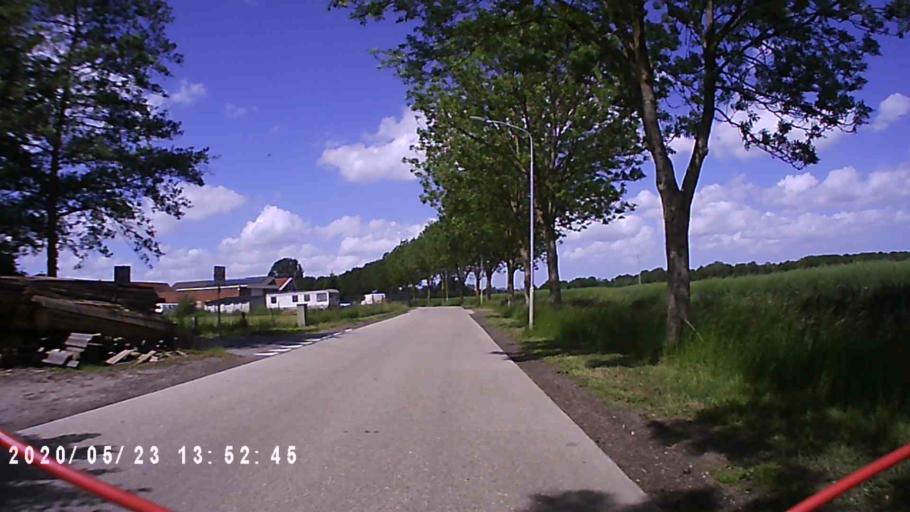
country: NL
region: Groningen
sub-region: Gemeente  Oldambt
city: Winschoten
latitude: 53.2686
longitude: 7.0375
